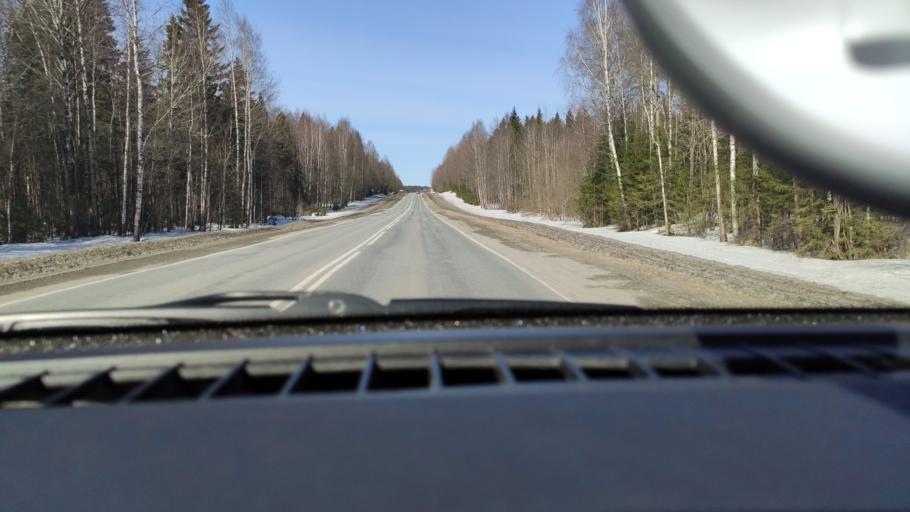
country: RU
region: Perm
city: Perm
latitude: 58.1482
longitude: 56.2597
